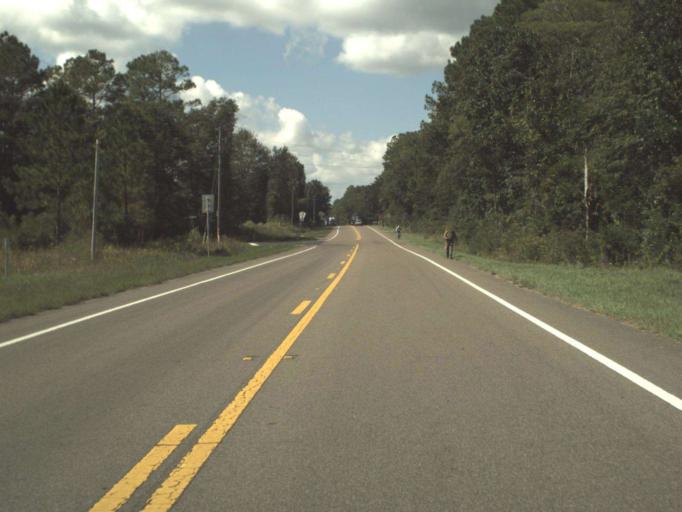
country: US
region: Florida
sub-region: Walton County
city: Freeport
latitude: 30.4706
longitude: -85.9580
